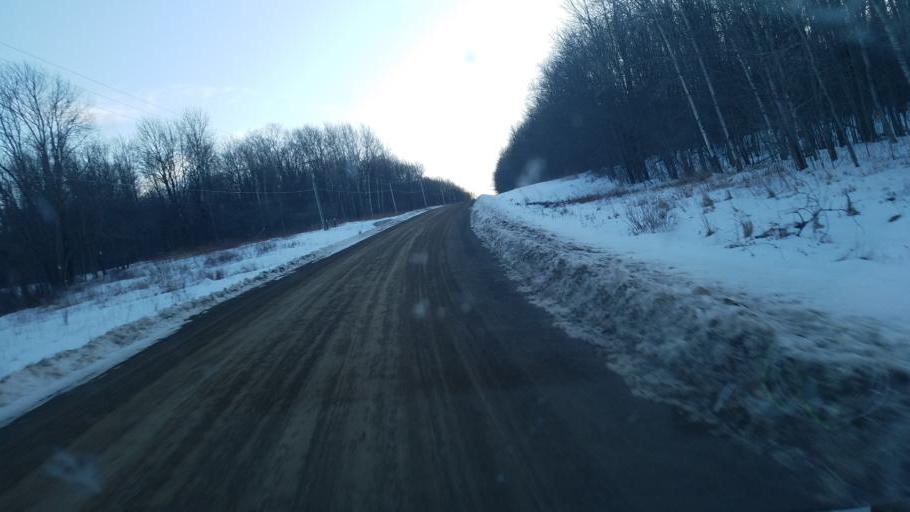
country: US
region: Pennsylvania
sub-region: Tioga County
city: Westfield
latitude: 42.0081
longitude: -77.6831
